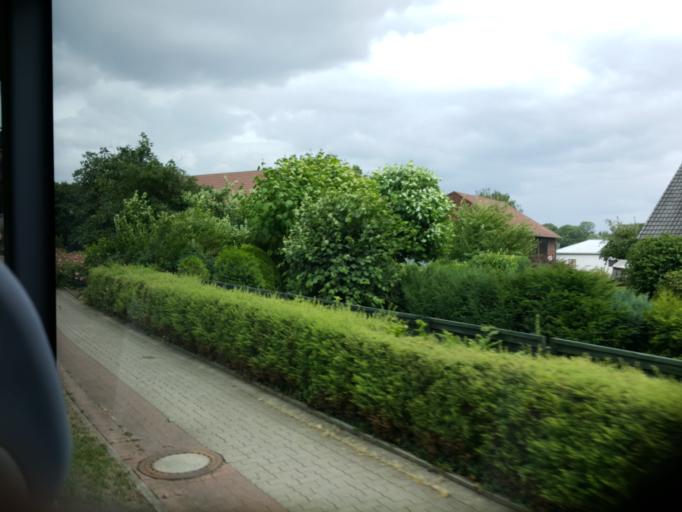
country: DE
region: North Rhine-Westphalia
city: Bad Oeynhausen
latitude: 52.2325
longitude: 8.8318
